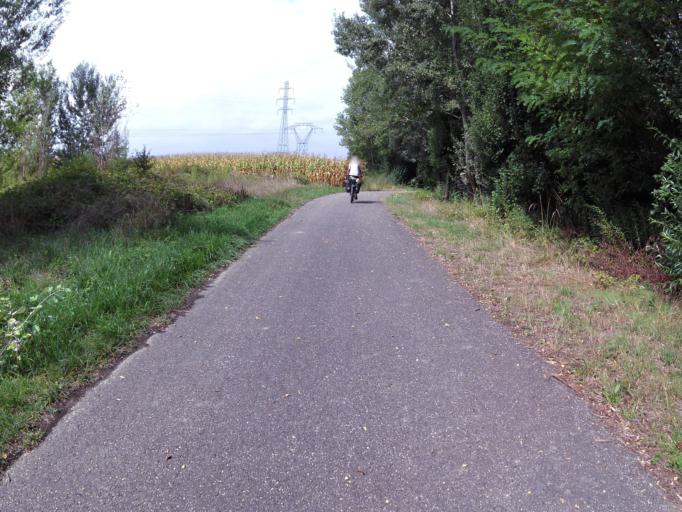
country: FR
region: Alsace
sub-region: Departement du Haut-Rhin
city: Biesheim
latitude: 48.0505
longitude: 7.5516
